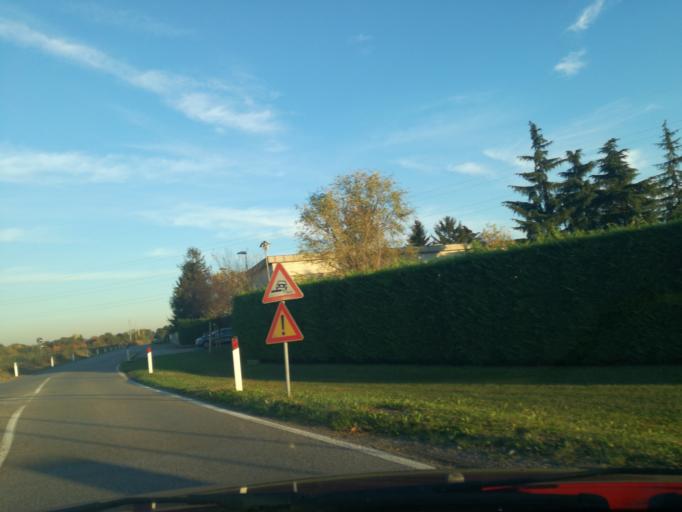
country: IT
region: Lombardy
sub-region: Provincia di Monza e Brianza
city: Burago di Molgora
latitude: 45.6061
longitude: 9.3808
